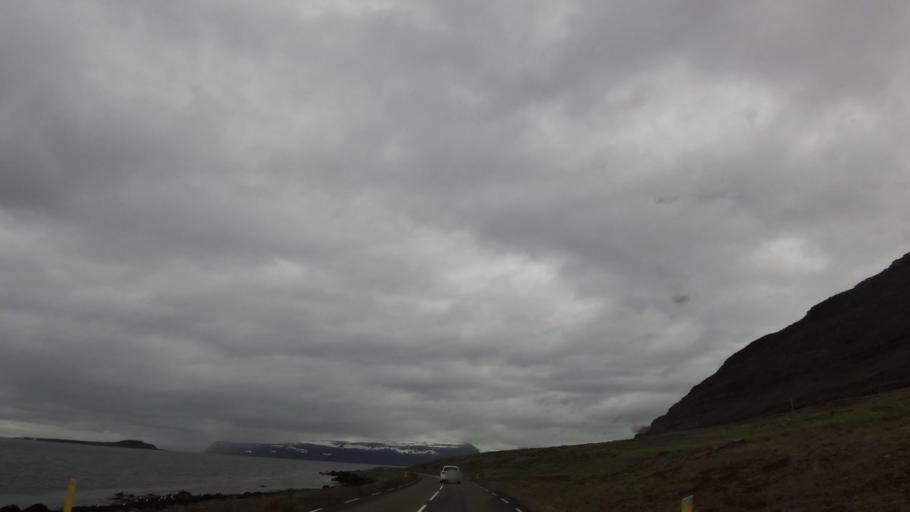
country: IS
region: Westfjords
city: Isafjoerdur
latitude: 66.0201
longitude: -22.7802
